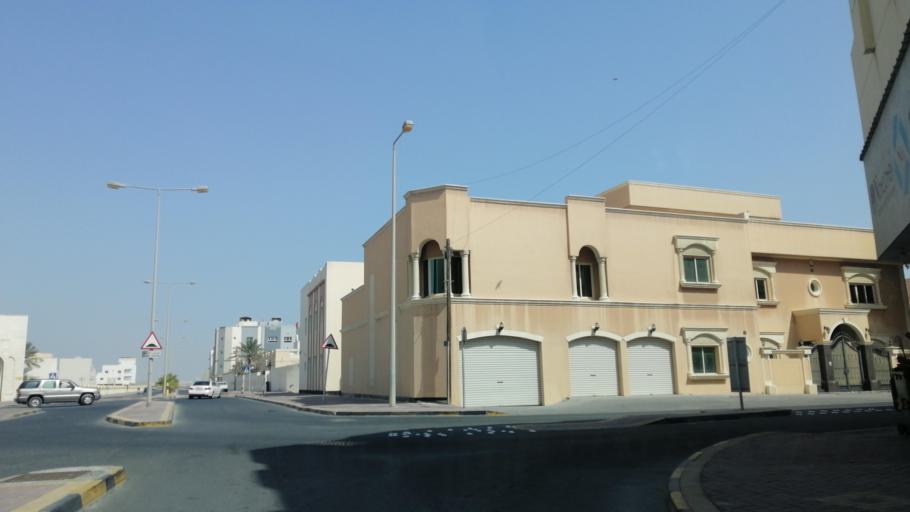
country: BH
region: Muharraq
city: Al Hadd
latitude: 26.2498
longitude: 50.6543
